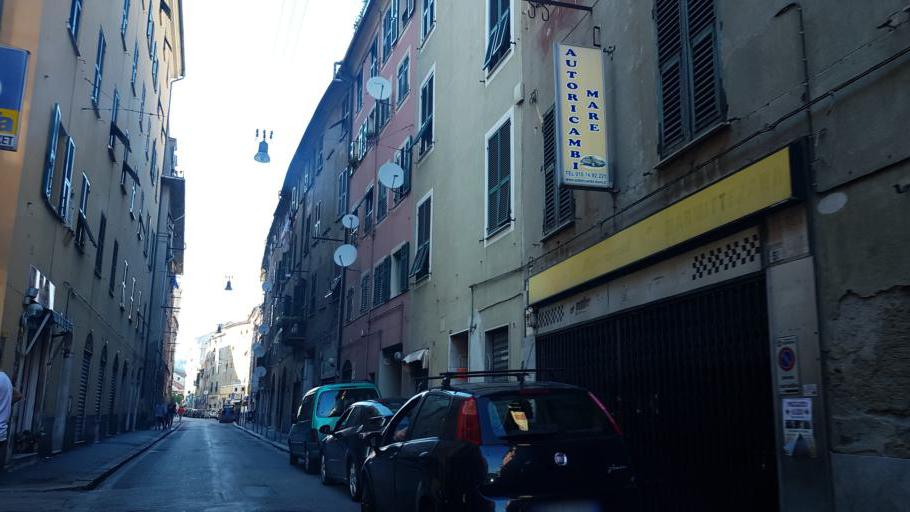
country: IT
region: Liguria
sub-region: Provincia di Genova
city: Genoa
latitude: 44.4384
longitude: 8.8922
